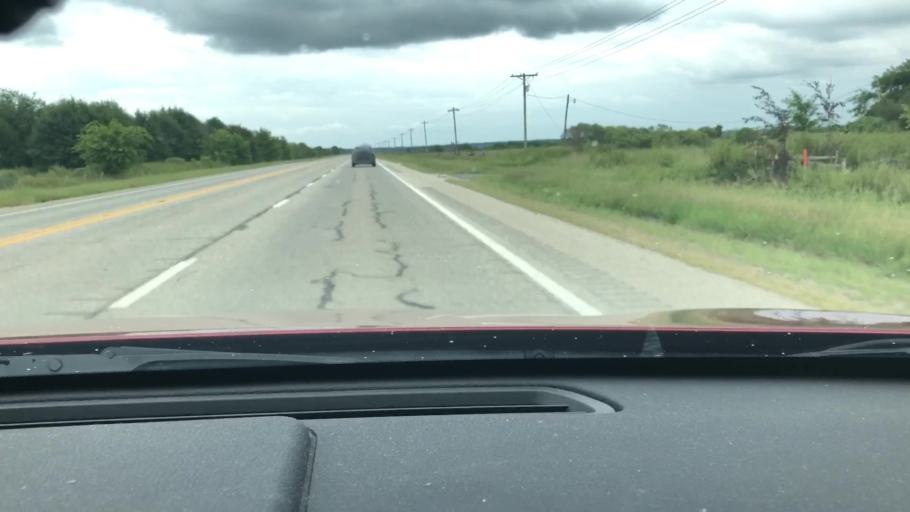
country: US
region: Arkansas
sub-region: Lafayette County
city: Lewisville
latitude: 33.4124
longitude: -93.7911
